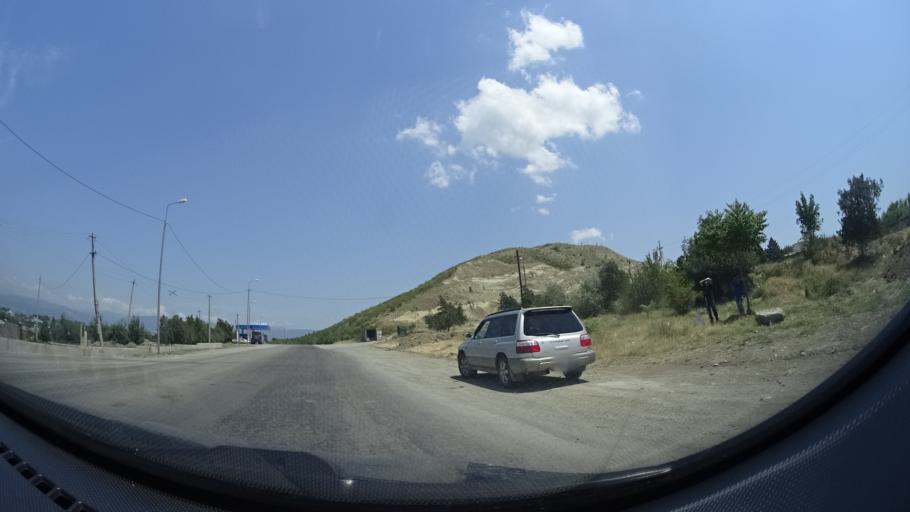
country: GE
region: Shida Kartli
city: Gori
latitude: 42.0079
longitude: 44.1285
